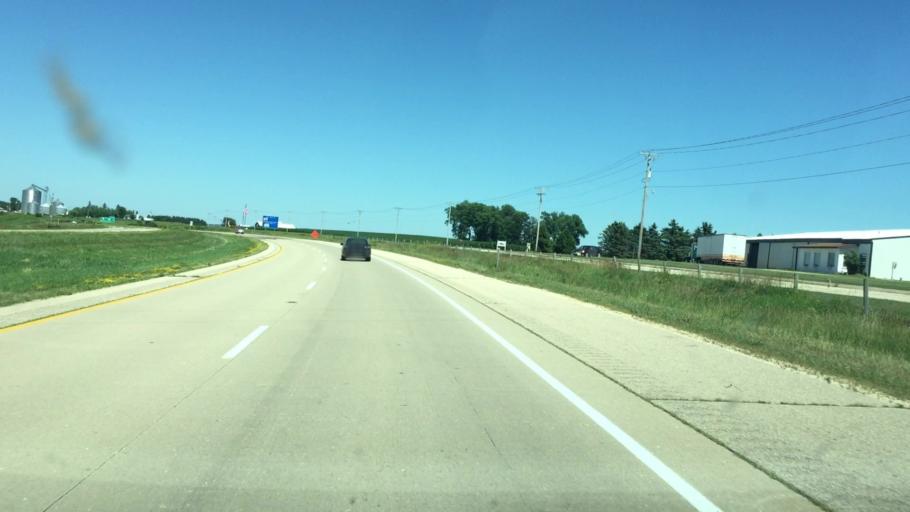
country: US
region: Wisconsin
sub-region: Iowa County
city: Mineral Point
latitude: 42.8411
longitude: -90.2052
